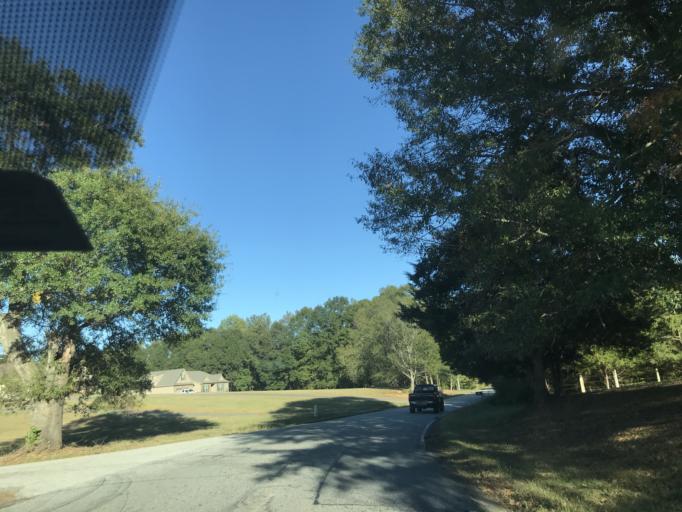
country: US
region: South Carolina
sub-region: Spartanburg County
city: Mayo
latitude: 35.1062
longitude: -81.8424
